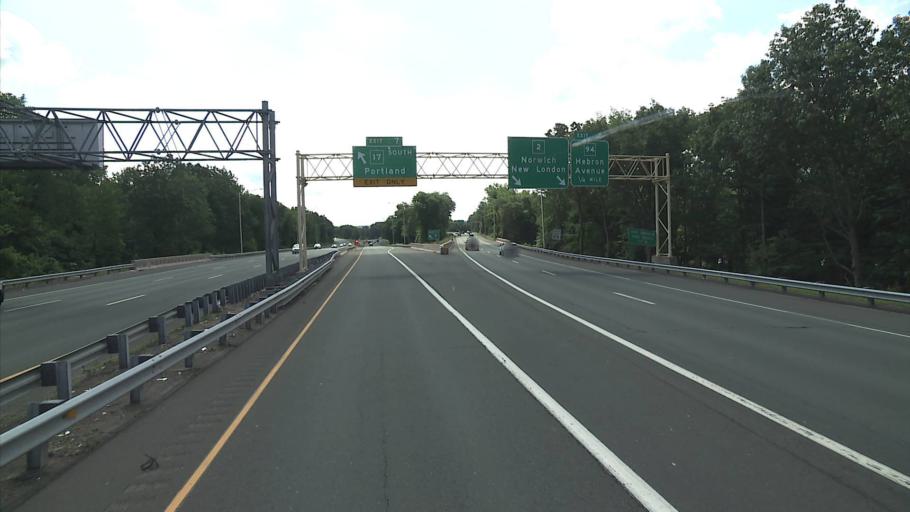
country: US
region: Connecticut
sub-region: Hartford County
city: Glastonbury
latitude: 41.7188
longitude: -72.6026
